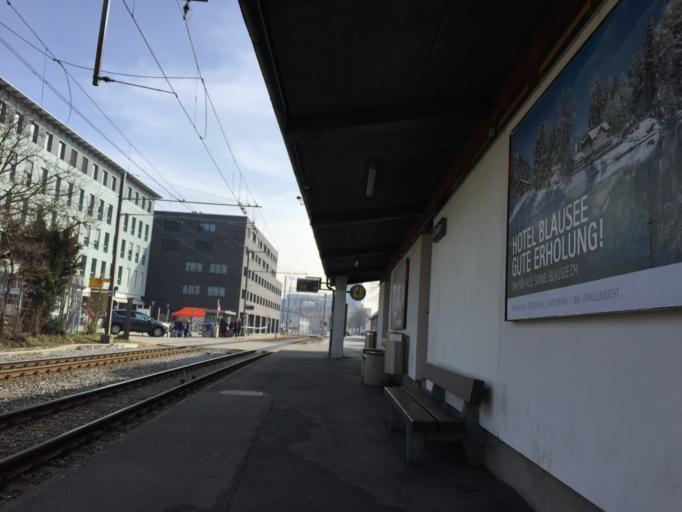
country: CH
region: Bern
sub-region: Bern-Mittelland District
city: Muri
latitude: 46.9346
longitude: 7.5053
